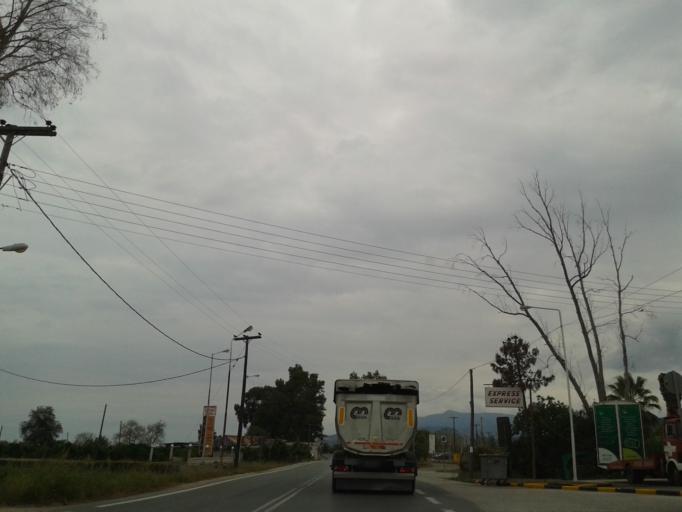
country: GR
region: Peloponnese
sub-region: Nomos Argolidos
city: Nea Kios
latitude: 37.6006
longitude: 22.7083
